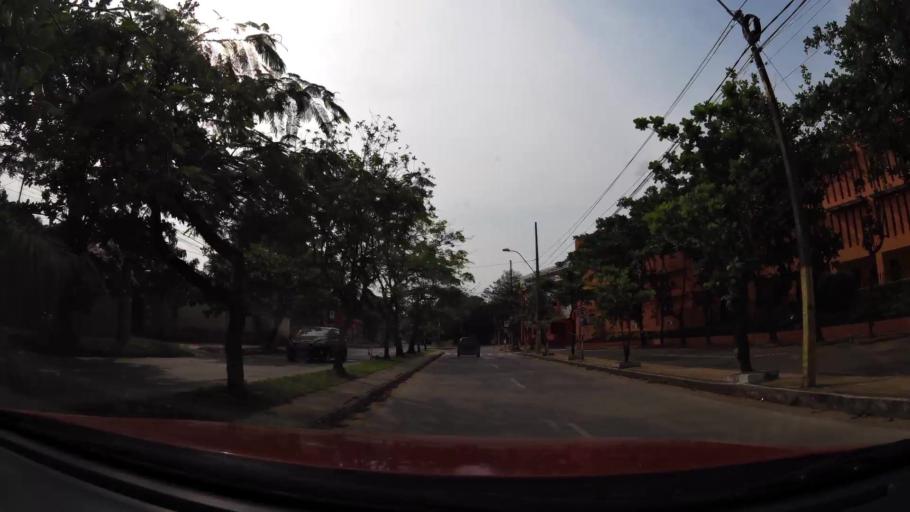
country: PY
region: Central
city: Fernando de la Mora
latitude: -25.2789
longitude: -57.5620
